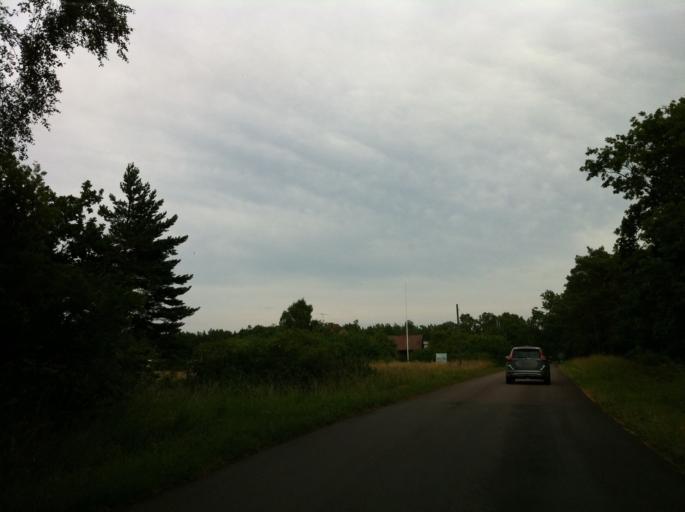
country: SE
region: Kalmar
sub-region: Vasterviks Kommun
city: Vaestervik
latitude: 57.3519
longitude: 17.0495
